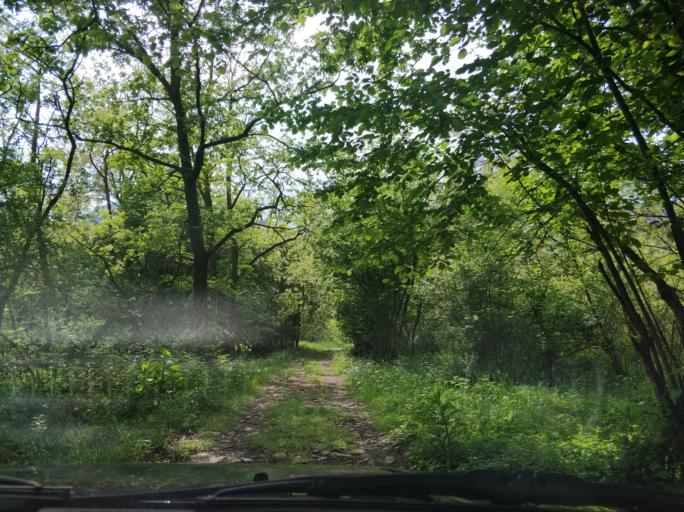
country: IT
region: Piedmont
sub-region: Provincia di Torino
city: Fiano
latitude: 45.1985
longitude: 7.5220
